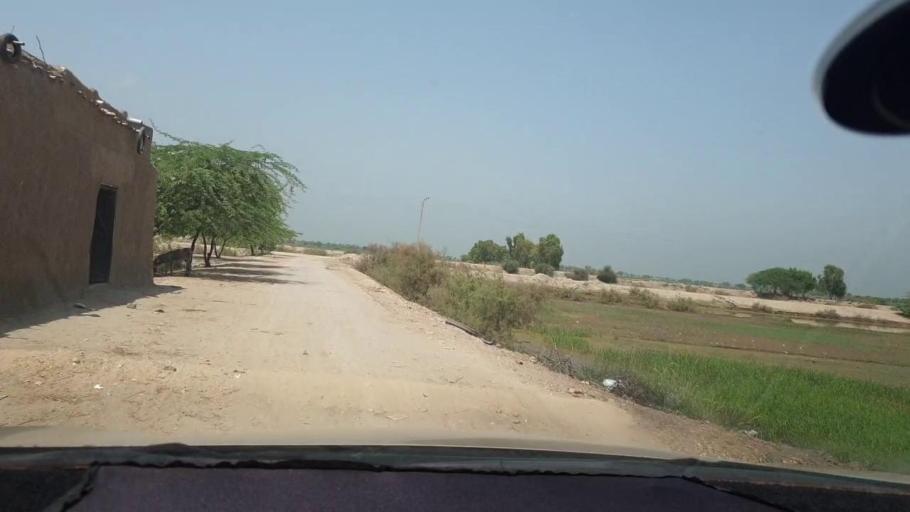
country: PK
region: Sindh
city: Kambar
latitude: 27.6764
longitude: 67.9099
